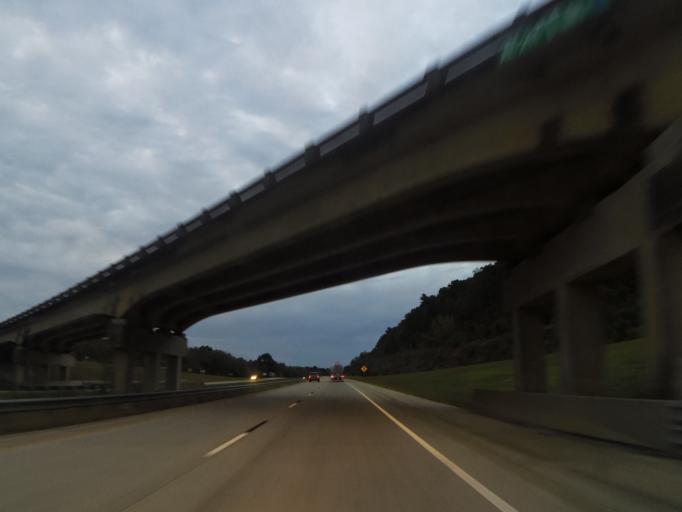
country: US
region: Alabama
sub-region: Etowah County
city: Gadsden
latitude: 34.0729
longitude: -86.0260
